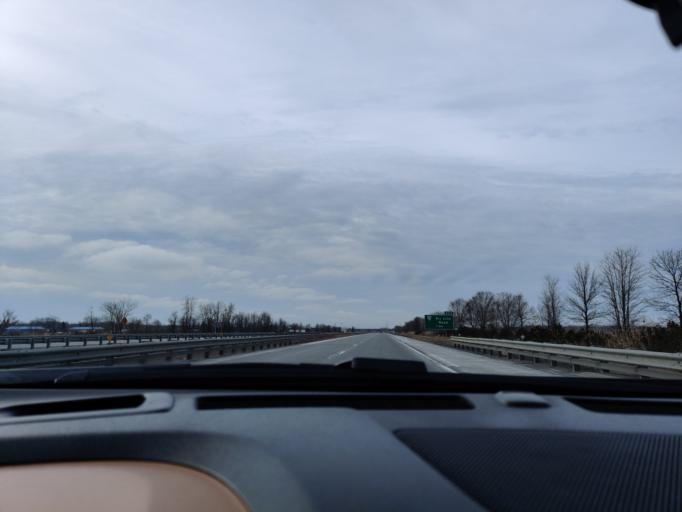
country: CA
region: Quebec
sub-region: Monteregie
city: Les Coteaux
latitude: 45.1981
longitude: -74.3699
